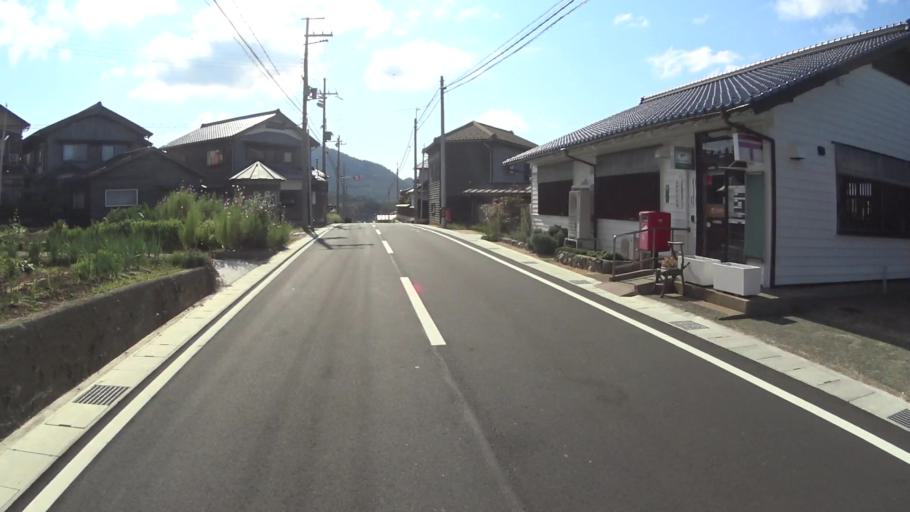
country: JP
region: Kyoto
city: Miyazu
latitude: 35.7585
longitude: 135.1786
